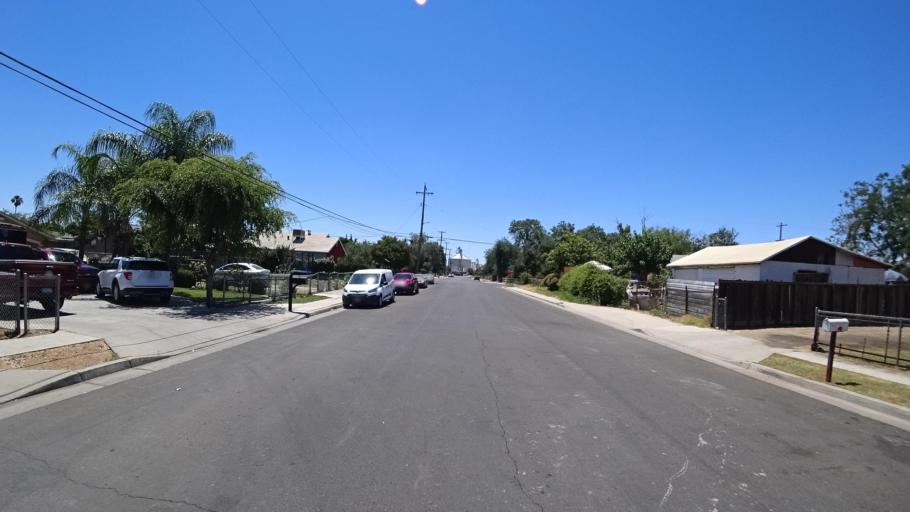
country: US
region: California
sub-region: Fresno County
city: Fresno
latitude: 36.7095
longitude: -119.7508
